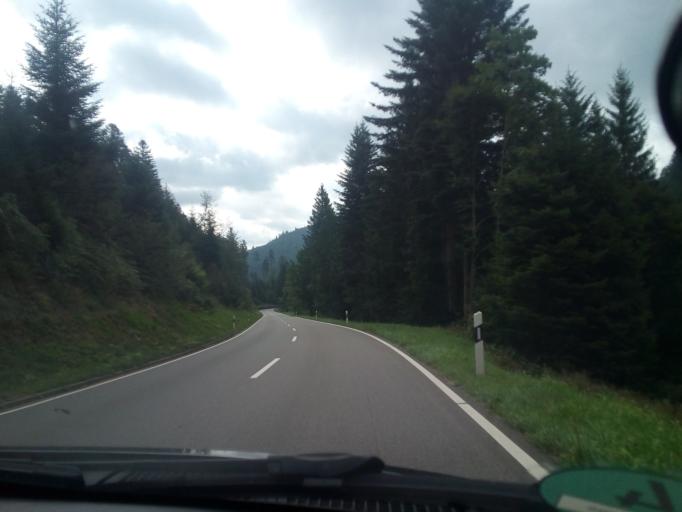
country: DE
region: Baden-Wuerttemberg
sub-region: Karlsruhe Region
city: Biberach
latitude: 48.5411
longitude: 8.2775
